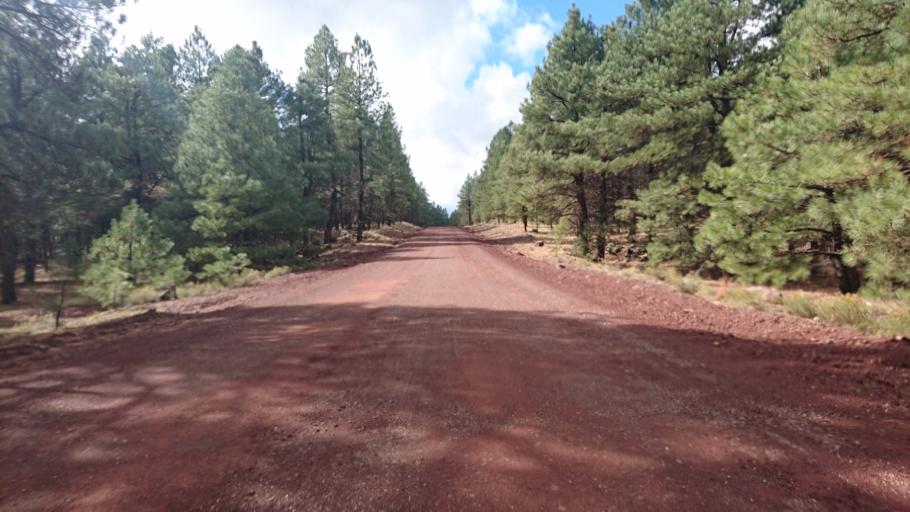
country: US
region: Arizona
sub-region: Coconino County
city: Parks
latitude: 35.2643
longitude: -111.9151
